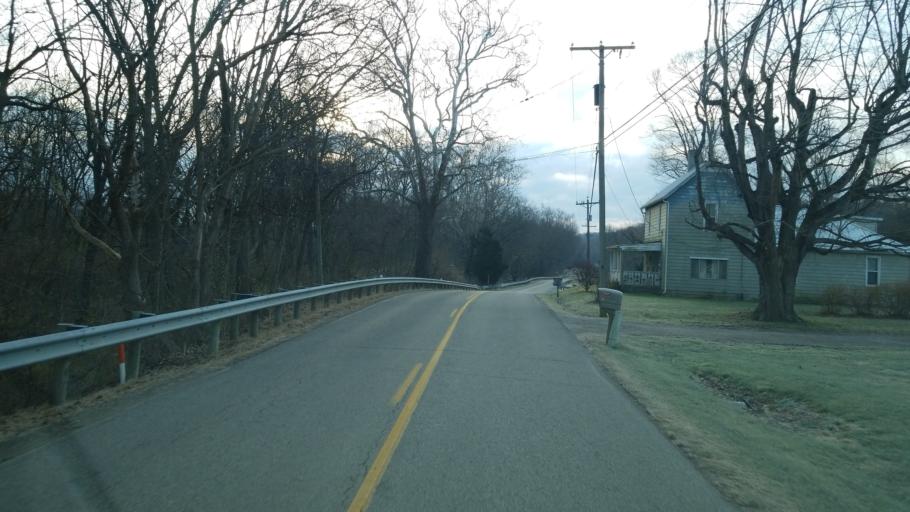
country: US
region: Ohio
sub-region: Ross County
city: Chillicothe
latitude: 39.2635
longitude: -82.9178
